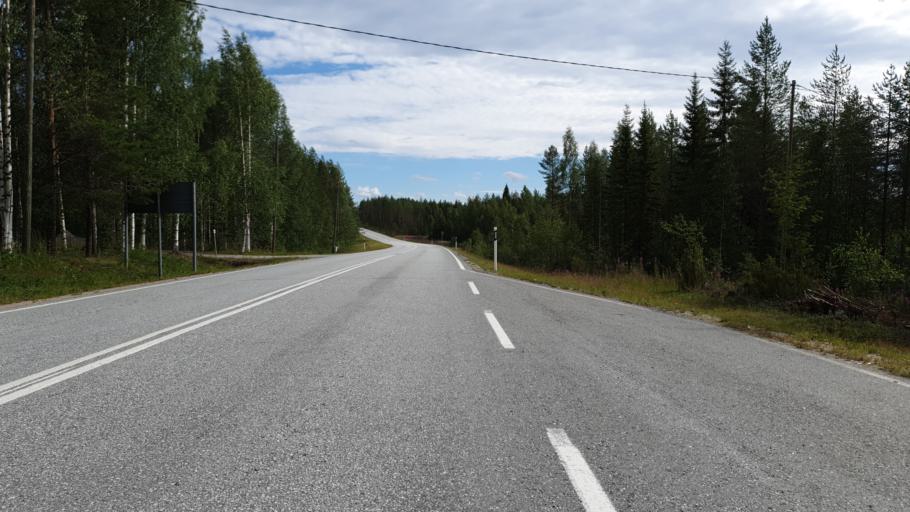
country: FI
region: Kainuu
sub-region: Kehys-Kainuu
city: Kuhmo
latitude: 64.4957
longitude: 29.9071
